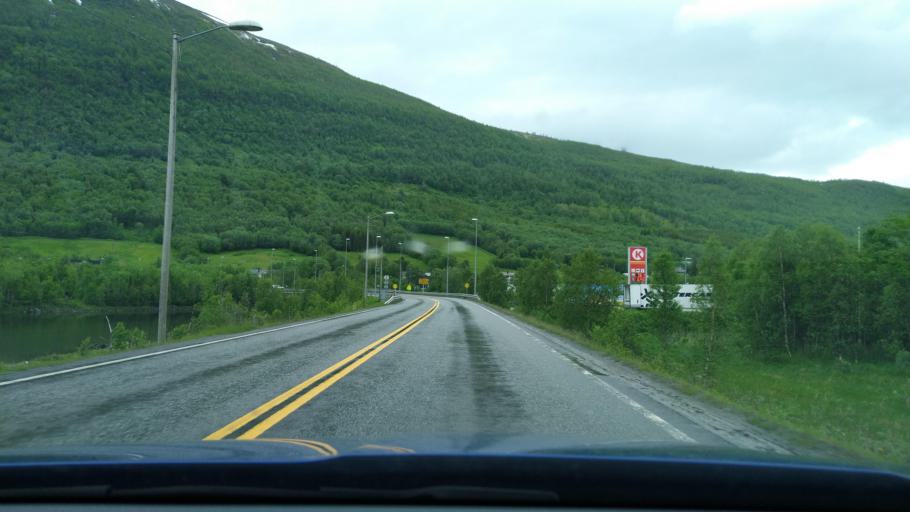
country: NO
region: Troms
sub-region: Balsfjord
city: Storsteinnes
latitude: 69.2168
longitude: 19.5542
